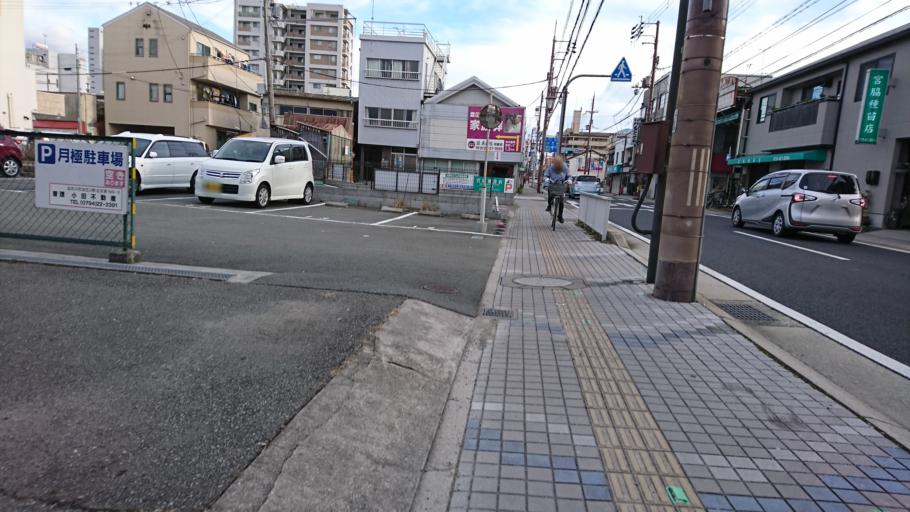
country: JP
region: Hyogo
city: Kakogawacho-honmachi
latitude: 34.7671
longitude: 134.8337
